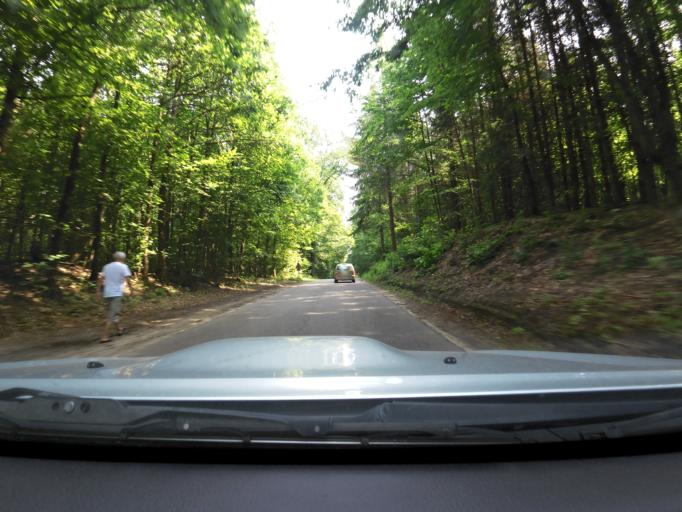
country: PL
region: Warmian-Masurian Voivodeship
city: Gierloz
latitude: 54.0785
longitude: 21.4859
